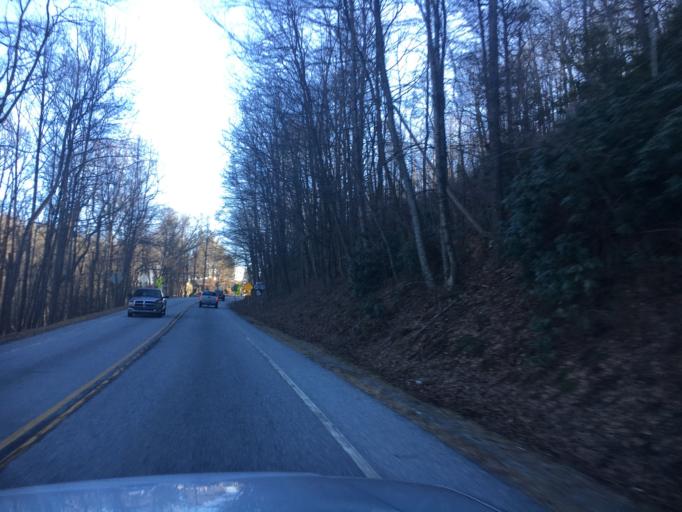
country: US
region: Georgia
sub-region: Union County
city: Blairsville
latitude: 34.7376
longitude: -83.9192
